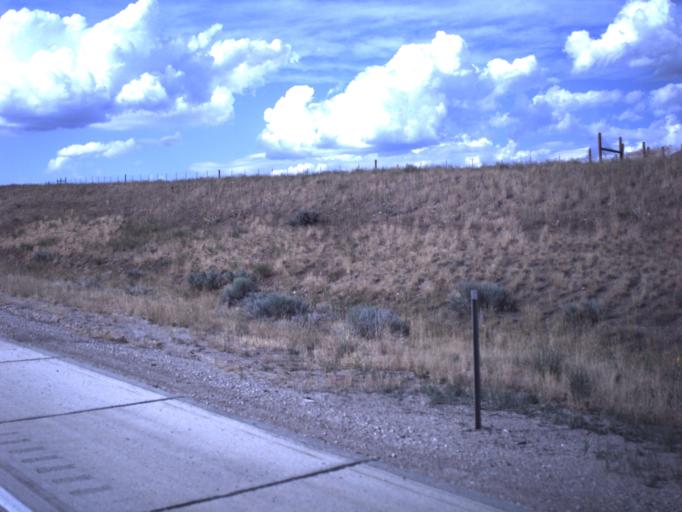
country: US
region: Utah
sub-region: Wasatch County
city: Heber
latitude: 40.5774
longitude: -111.4353
